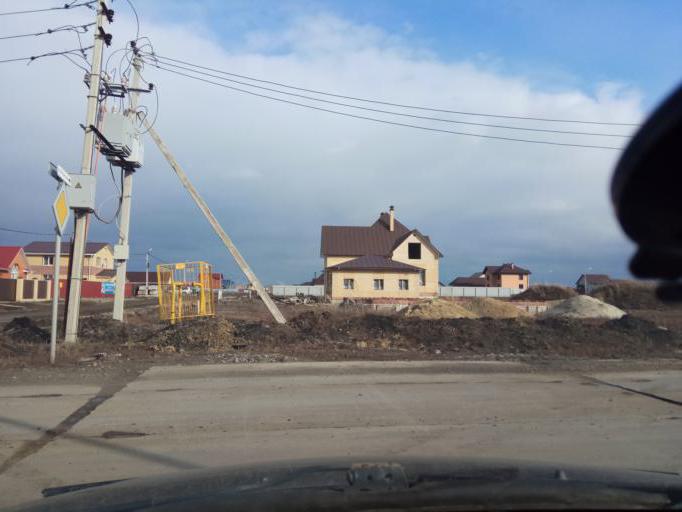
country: RU
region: Tjumen
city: Moskovskiy
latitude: 57.2152
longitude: 65.2575
